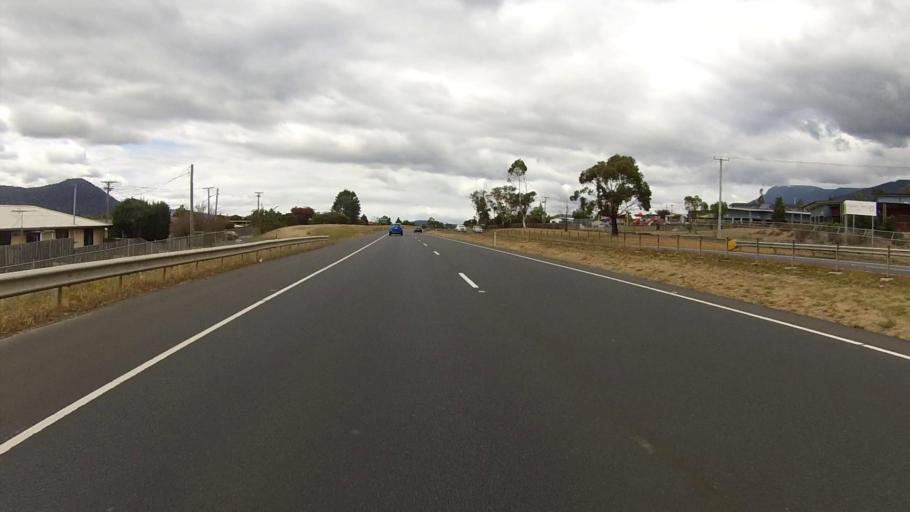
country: AU
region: Tasmania
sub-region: Glenorchy
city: Claremont
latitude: -42.7835
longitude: 147.2404
